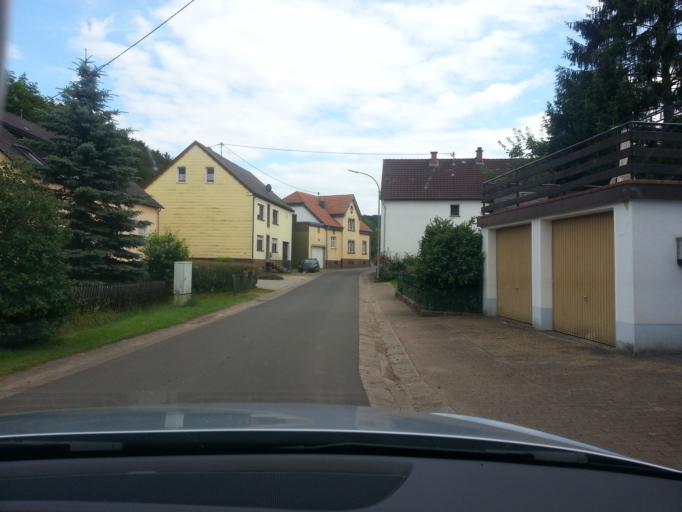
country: DE
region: Saarland
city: Marpingen
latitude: 49.4373
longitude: 7.0278
